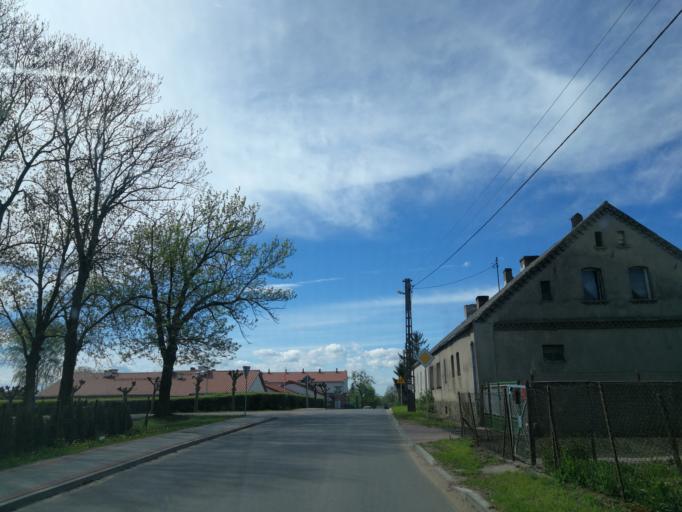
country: PL
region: Warmian-Masurian Voivodeship
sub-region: Powiat ilawski
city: Lubawa
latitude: 53.5981
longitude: 19.7015
